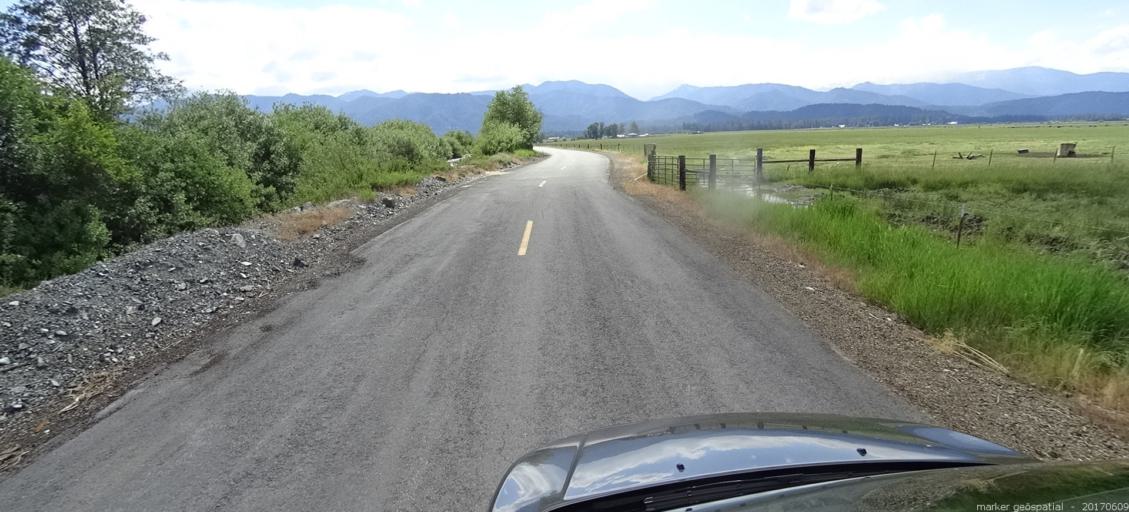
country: US
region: California
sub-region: Siskiyou County
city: Yreka
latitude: 41.5145
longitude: -122.8731
